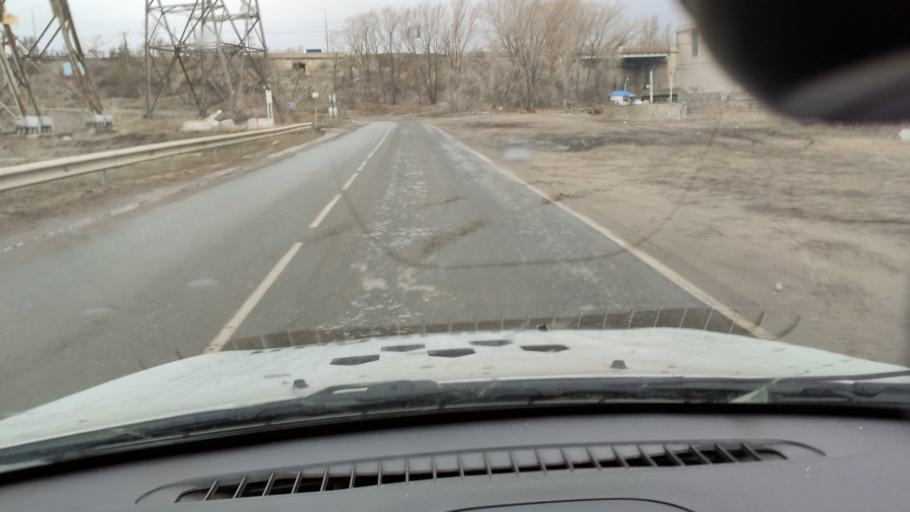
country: RU
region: Samara
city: Zhigulevsk
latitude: 53.4628
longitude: 49.5055
